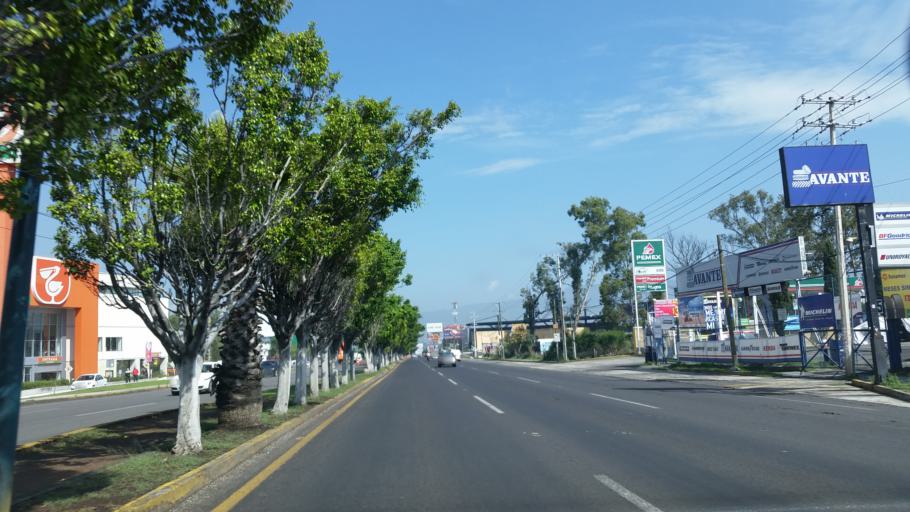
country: MX
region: Michoacan
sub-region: Morelia
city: Morelos
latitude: 19.6725
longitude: -101.2105
